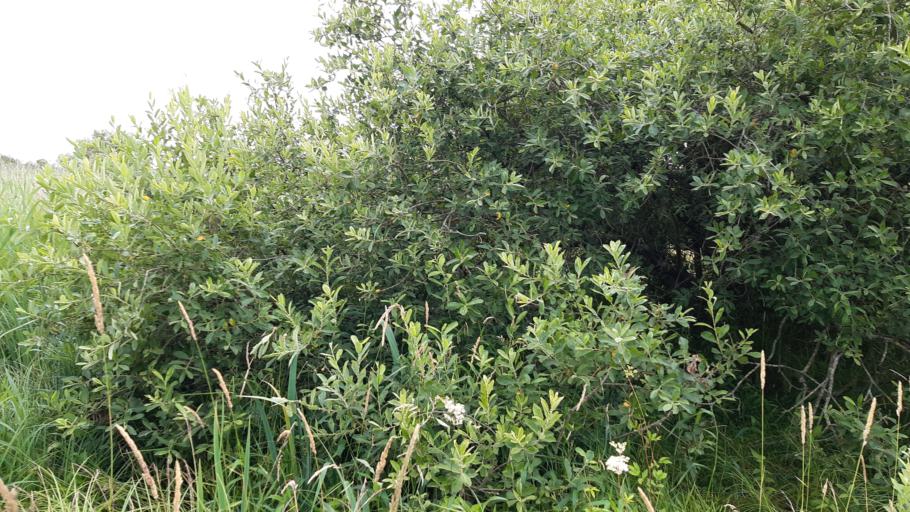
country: DK
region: Capital Region
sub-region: Ballerup Kommune
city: Malov
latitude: 55.7263
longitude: 12.3294
